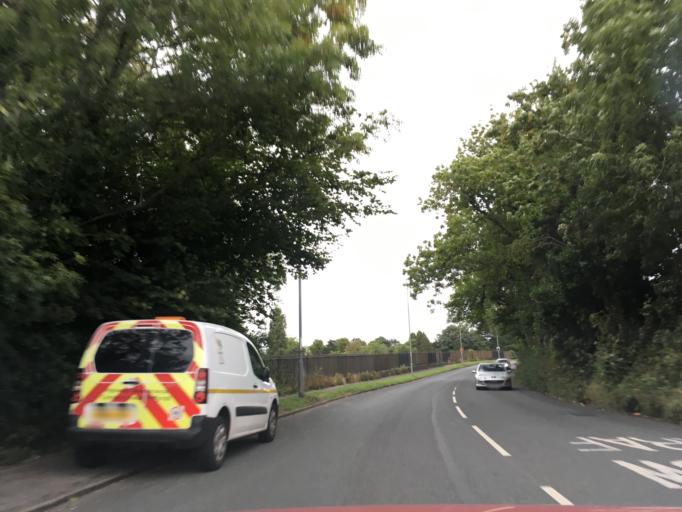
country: GB
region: Wales
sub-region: Newport
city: Newport
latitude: 51.5797
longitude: -3.0251
